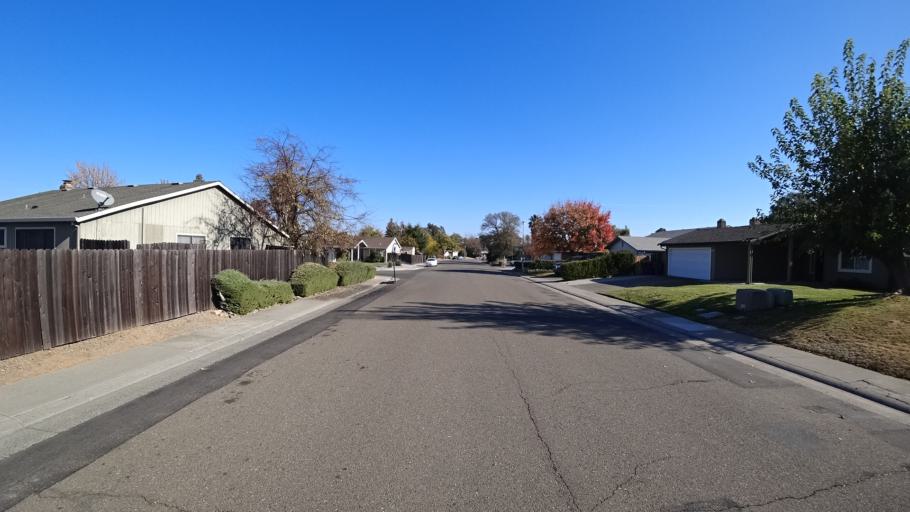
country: US
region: California
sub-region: Sacramento County
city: Antelope
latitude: 38.7107
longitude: -121.3147
